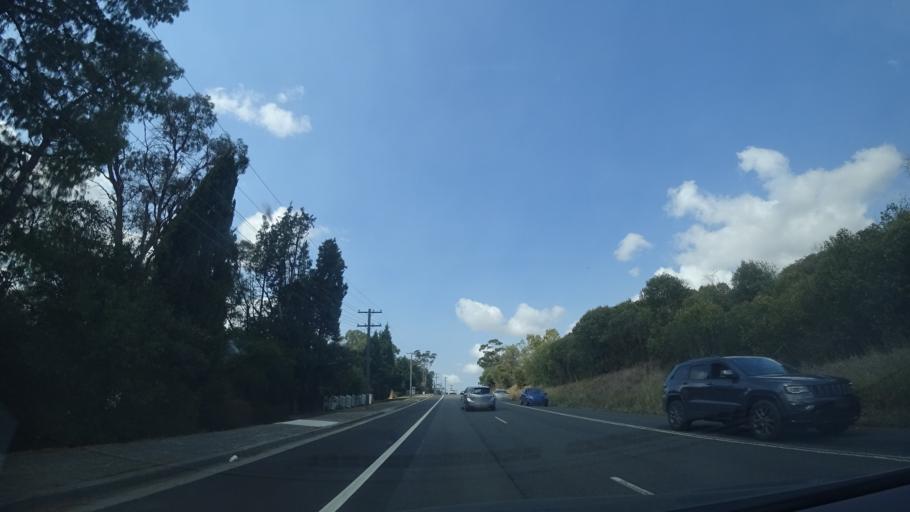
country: AU
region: New South Wales
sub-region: Wollondilly
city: Picton
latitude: -34.1811
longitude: 150.6081
